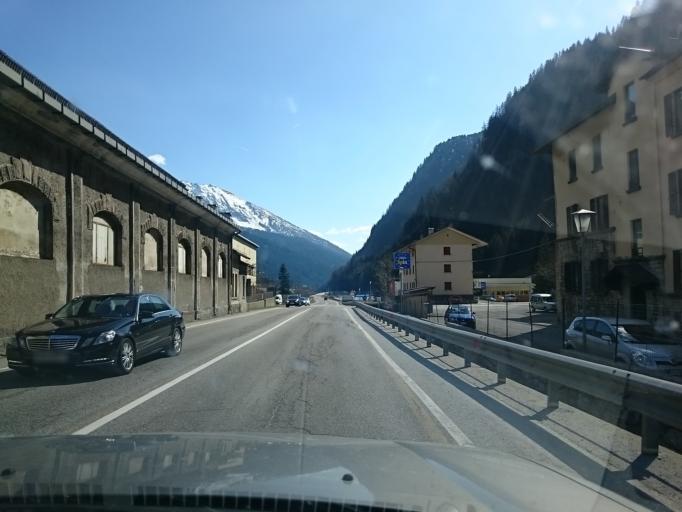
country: AT
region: Tyrol
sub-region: Politischer Bezirk Innsbruck Land
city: Gries am Brenner
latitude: 47.0013
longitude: 11.5040
